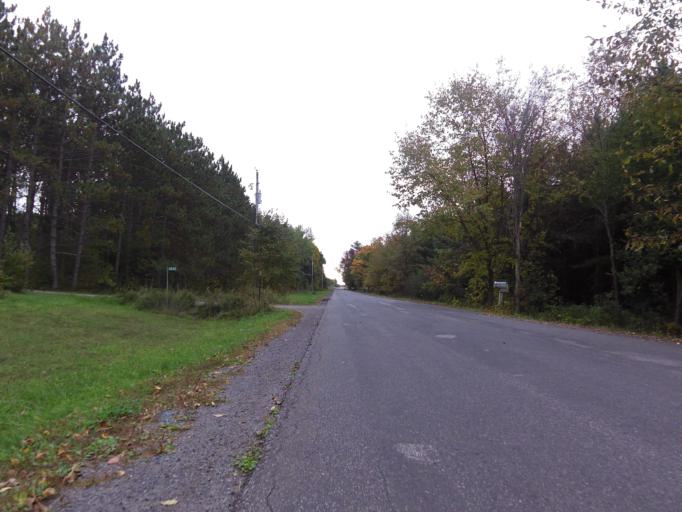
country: CA
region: Ontario
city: Arnprior
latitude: 45.4727
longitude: -76.1575
